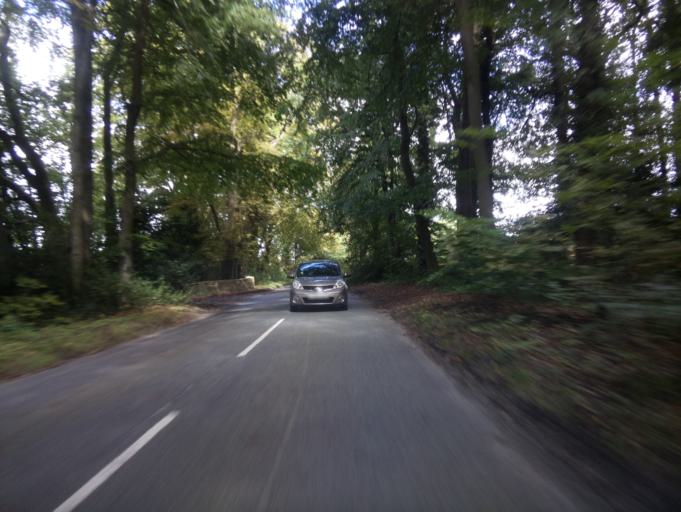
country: GB
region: England
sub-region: Wiltshire
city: Colerne
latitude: 51.4581
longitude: -2.2553
